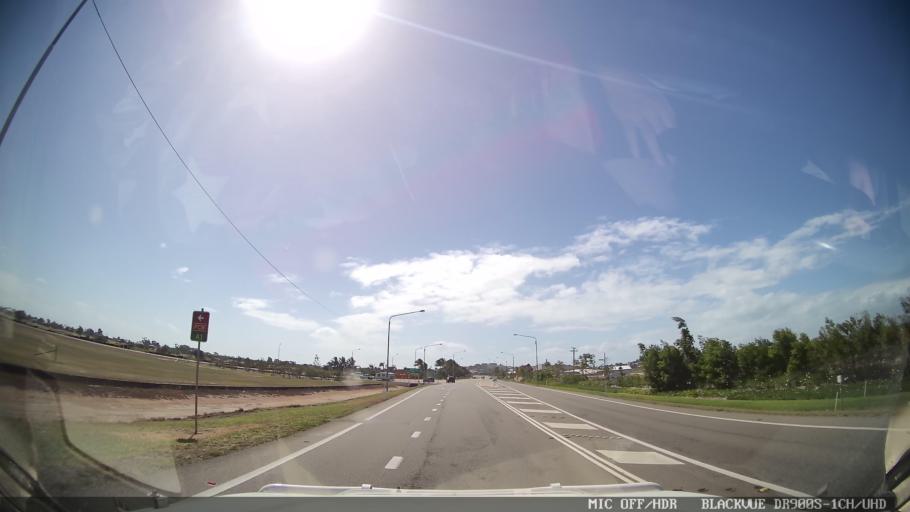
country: AU
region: Queensland
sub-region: Whitsunday
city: Bowen
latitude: -20.0160
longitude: 148.2203
